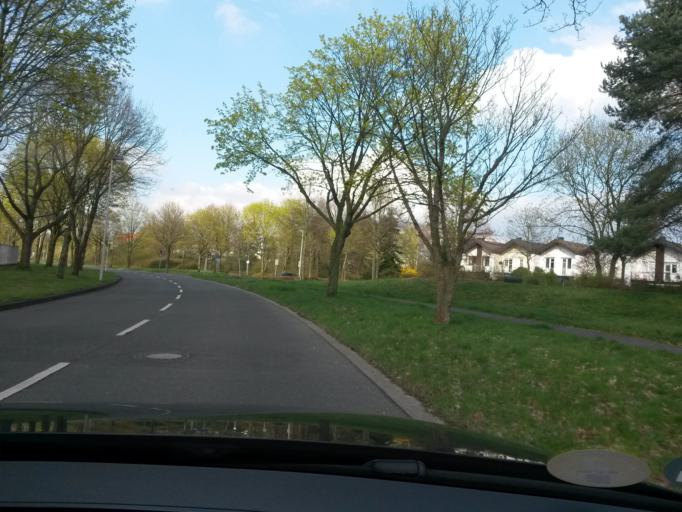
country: DE
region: North Rhine-Westphalia
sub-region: Regierungsbezirk Koln
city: Alfter
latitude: 50.6982
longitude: 7.0506
